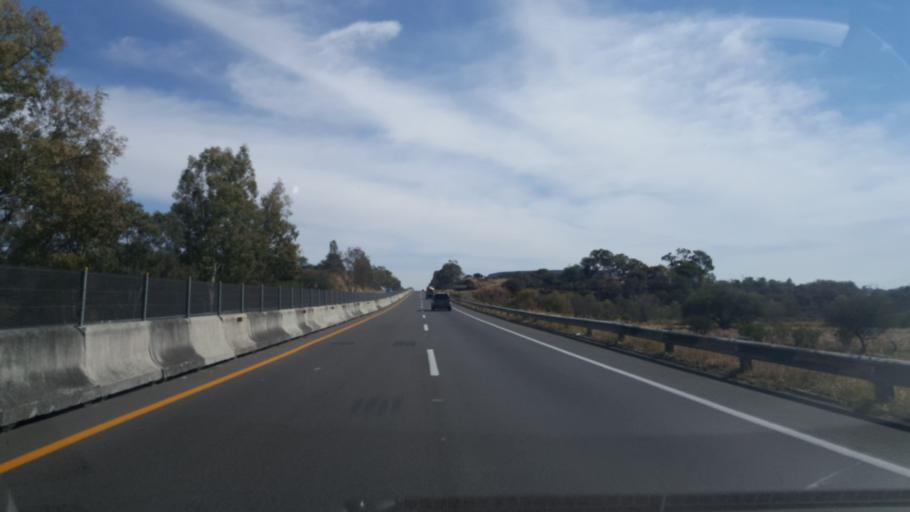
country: MX
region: Jalisco
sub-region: Lagos de Moreno
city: Cristeros [Fraccionamiento]
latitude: 21.3104
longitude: -102.0318
